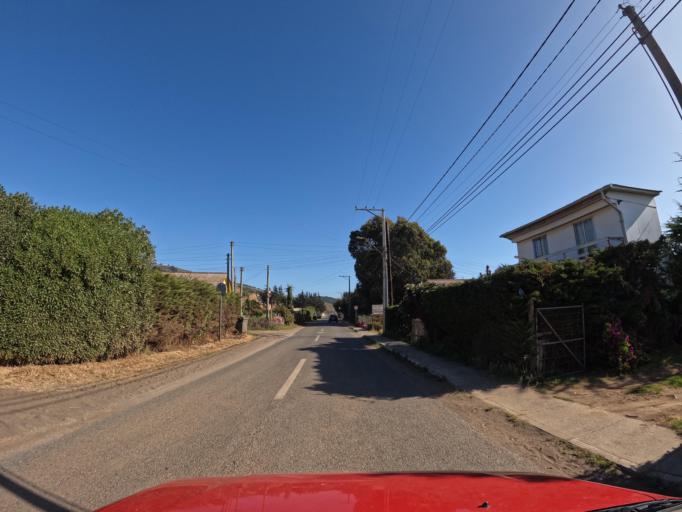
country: CL
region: Maule
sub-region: Provincia de Talca
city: Constitucion
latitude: -34.8477
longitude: -72.1413
